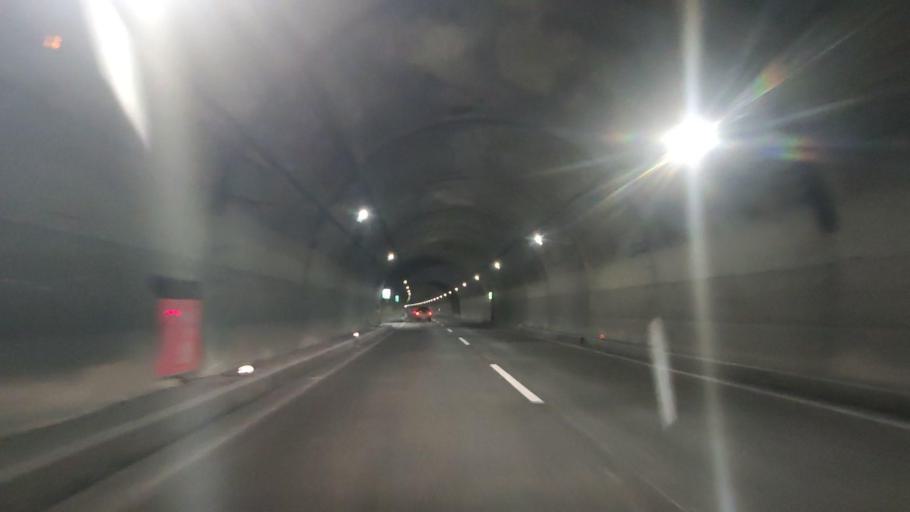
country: JP
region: Oita
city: Beppu
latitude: 33.2723
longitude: 131.3422
